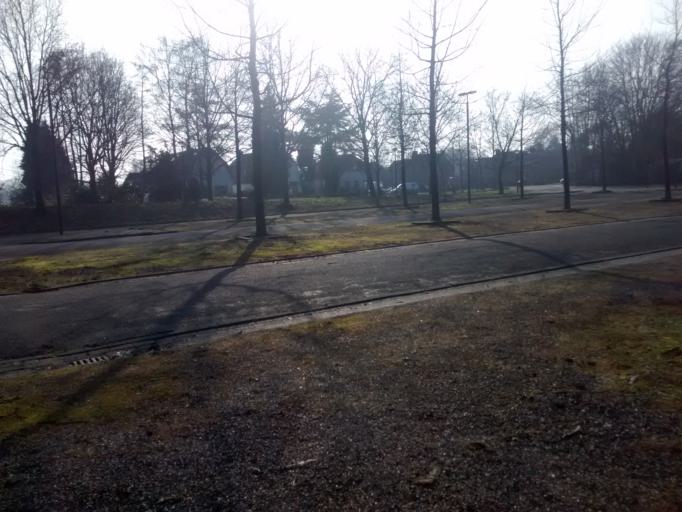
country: NL
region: Utrecht
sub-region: Gemeente Nieuwegein
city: Nieuwegein
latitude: 52.0120
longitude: 5.0884
